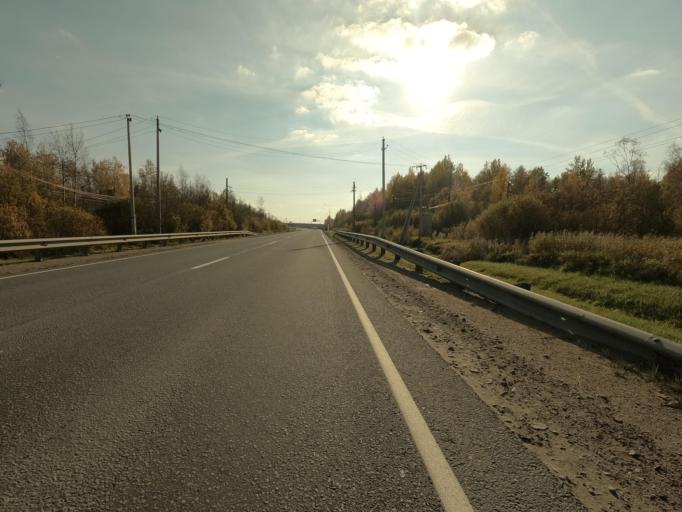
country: RU
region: Leningrad
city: Mga
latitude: 59.7639
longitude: 31.0950
